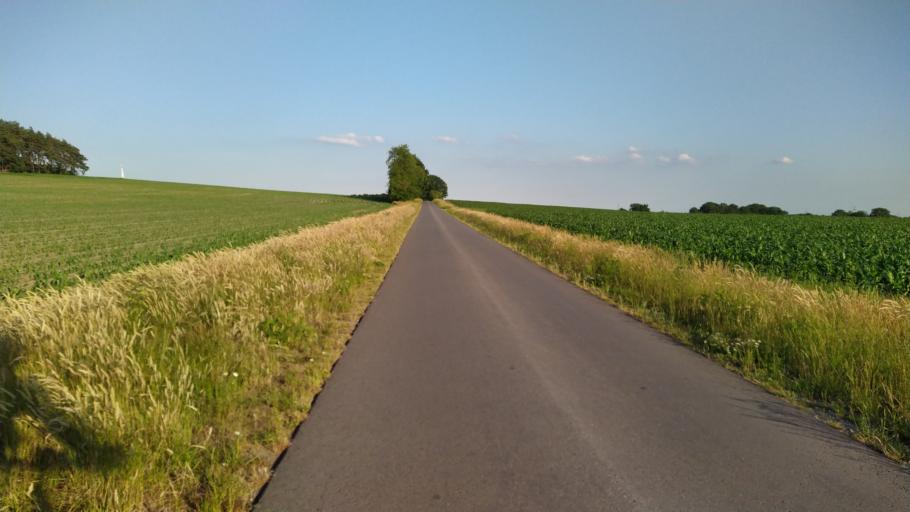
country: DE
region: Lower Saxony
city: Alfstedt
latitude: 53.5692
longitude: 9.0243
